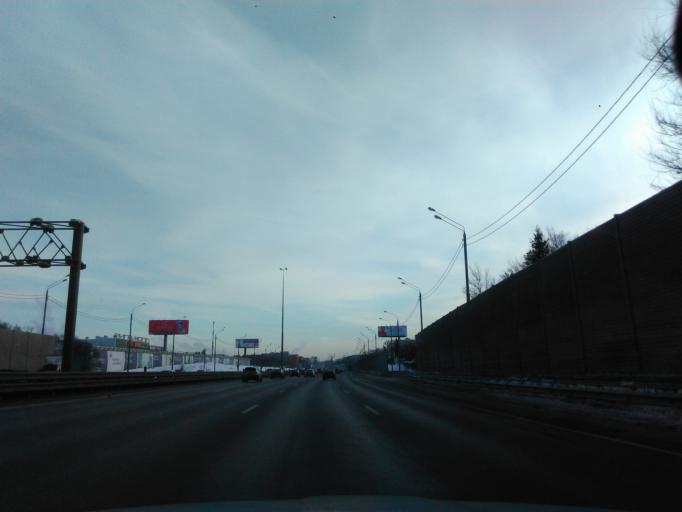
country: RU
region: Moskovskaya
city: Arkhangel'skoye
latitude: 55.7956
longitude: 37.2691
